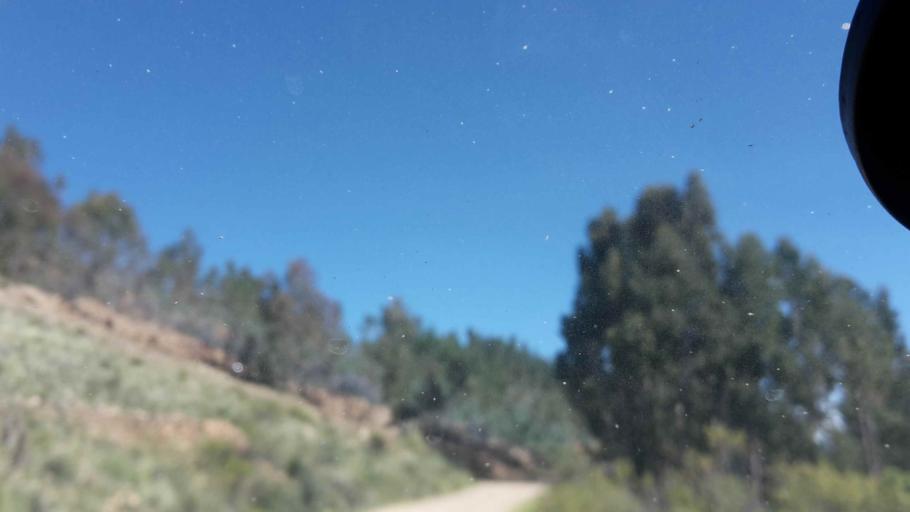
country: BO
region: Cochabamba
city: Arani
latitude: -17.6815
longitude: -65.7234
